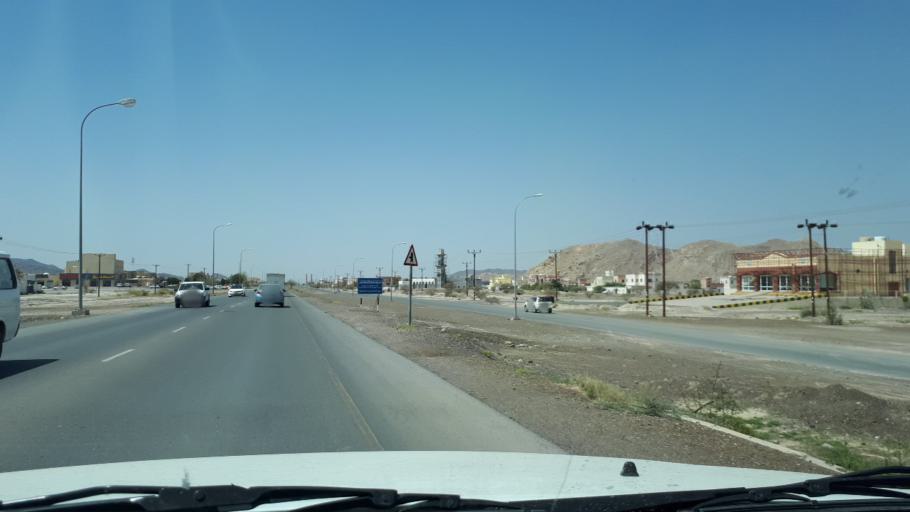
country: OM
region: Muhafazat ad Dakhiliyah
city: Bahla'
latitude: 23.0160
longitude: 57.3277
